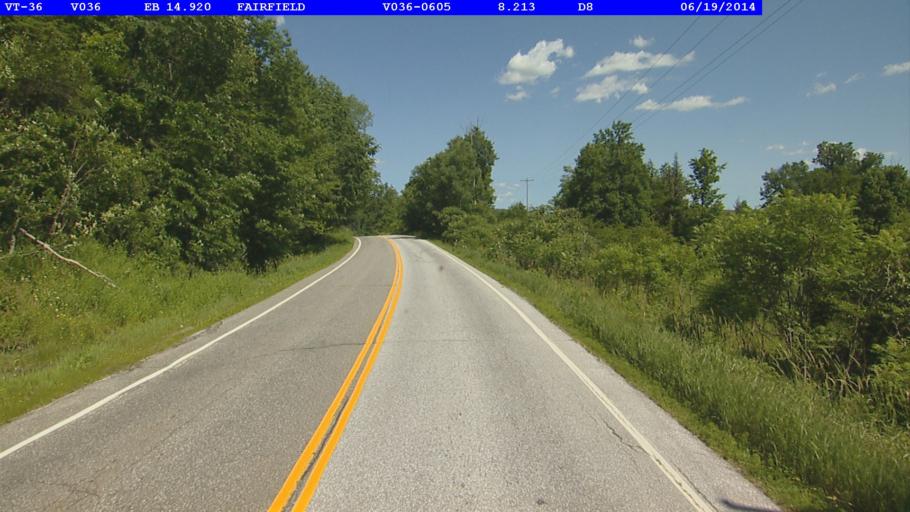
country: US
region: Vermont
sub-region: Franklin County
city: Enosburg Falls
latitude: 44.7940
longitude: -72.8784
